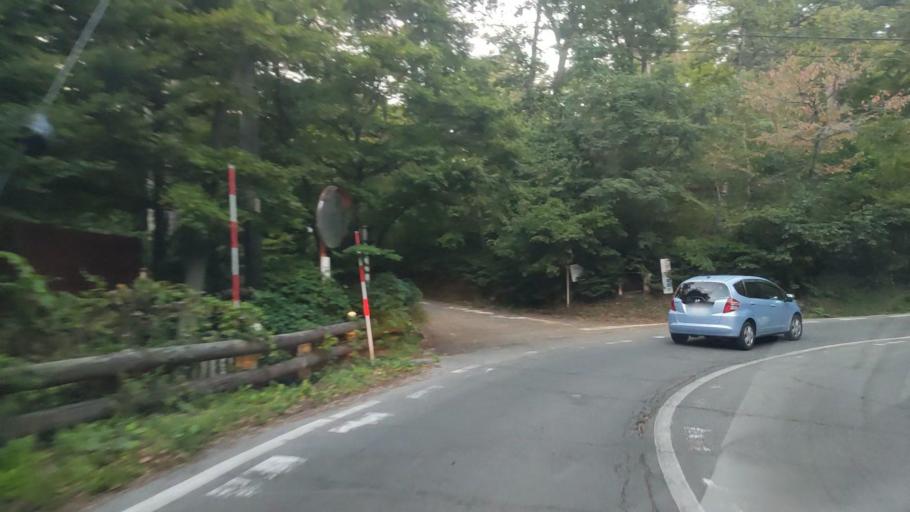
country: JP
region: Nagano
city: Komoro
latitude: 36.3798
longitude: 138.5844
